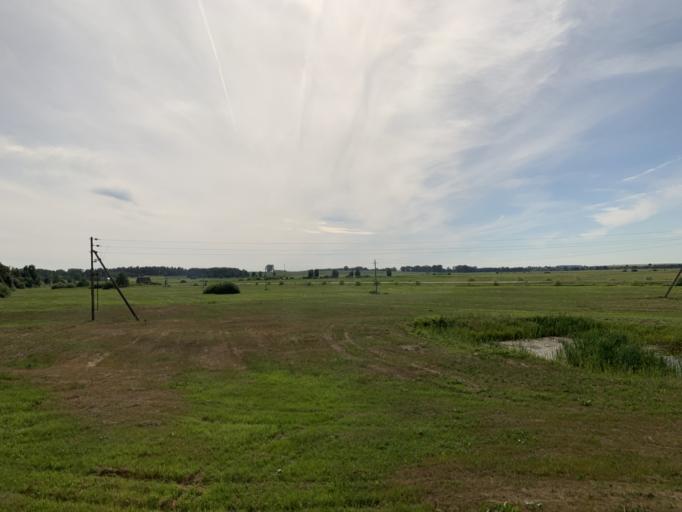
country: BY
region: Minsk
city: Novy Svyerzhan'
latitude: 53.4667
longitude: 26.7277
